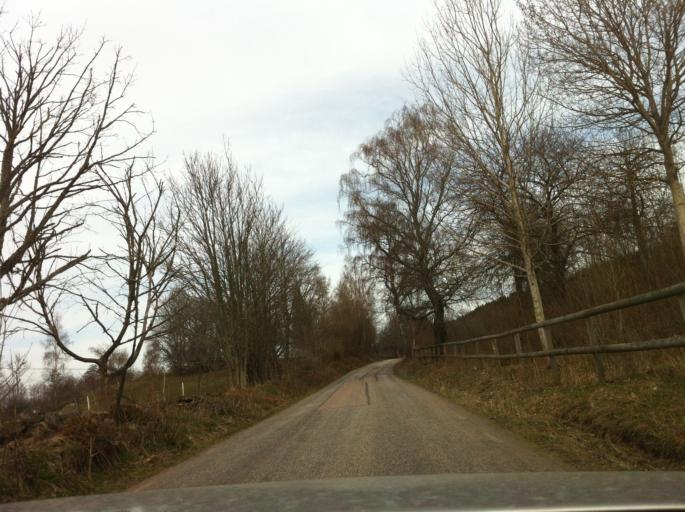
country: SE
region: Vaestra Goetaland
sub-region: Skara Kommun
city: Axvall
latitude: 58.4241
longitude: 13.6837
